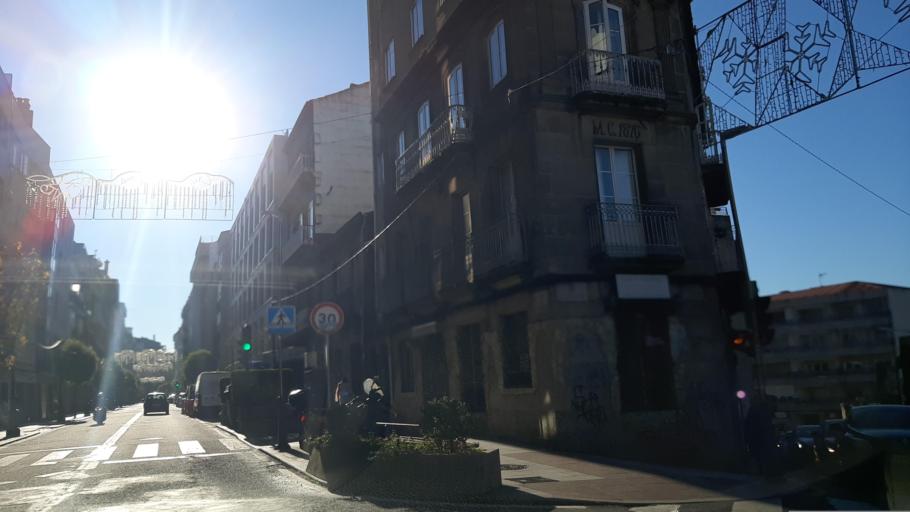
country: ES
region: Galicia
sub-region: Provincia de Pontevedra
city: Vigo
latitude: 42.2351
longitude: -8.7292
